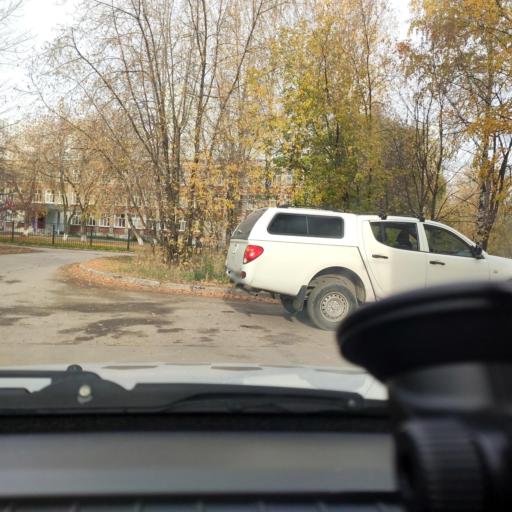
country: RU
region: Perm
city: Perm
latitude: 57.9877
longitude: 56.2711
